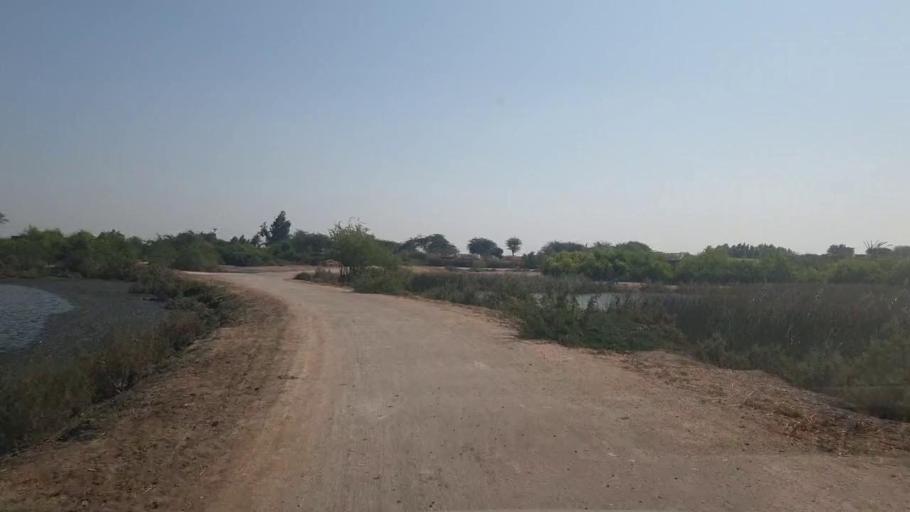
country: PK
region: Sindh
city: Badin
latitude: 24.6396
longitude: 68.9131
